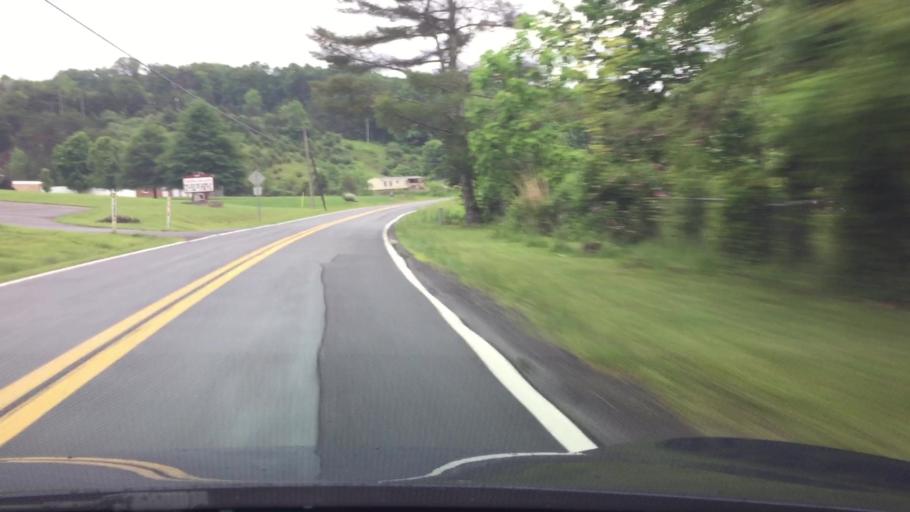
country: US
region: West Virginia
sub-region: Summers County
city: Hinton
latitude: 37.5788
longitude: -80.7884
